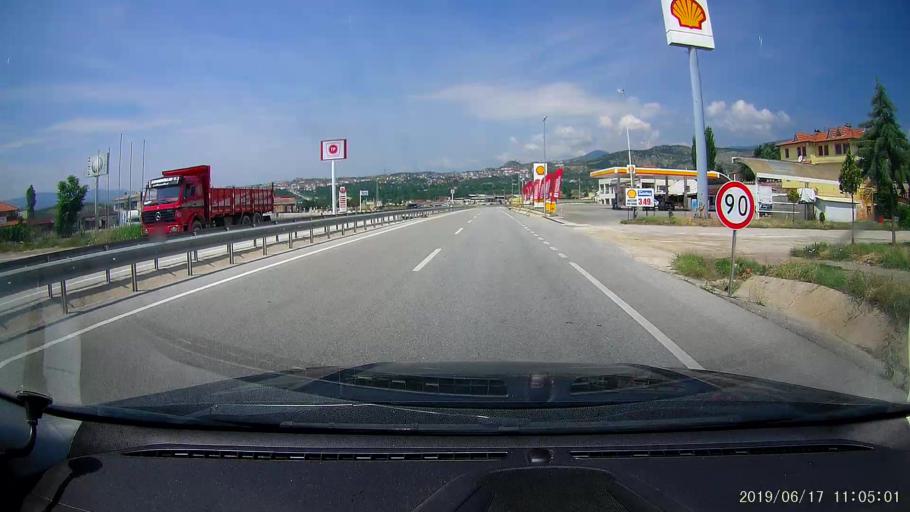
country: TR
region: Kastamonu
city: Tosya
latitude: 41.0187
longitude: 34.0819
